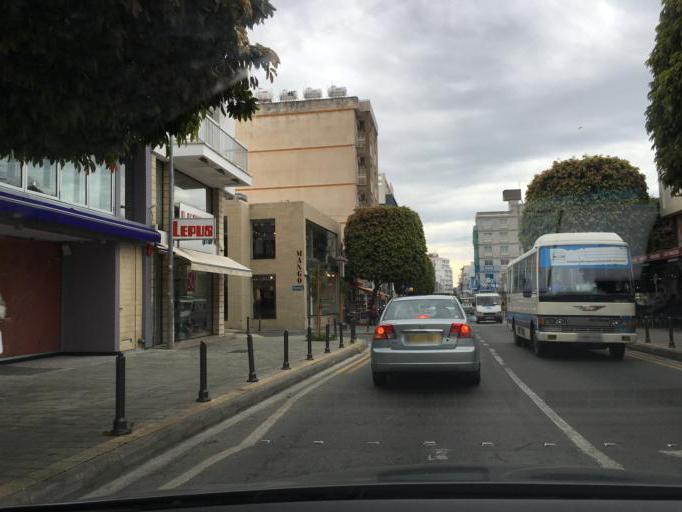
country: CY
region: Limassol
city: Limassol
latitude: 34.6798
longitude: 33.0438
